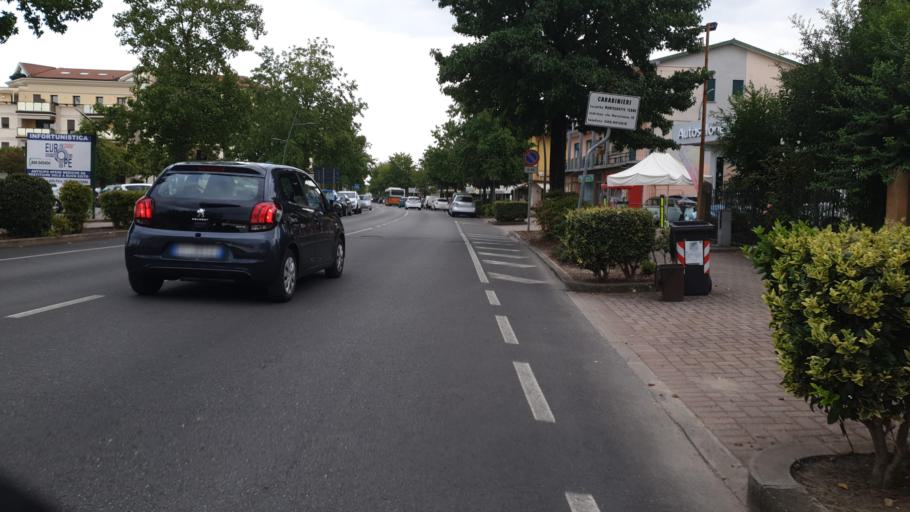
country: IT
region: Veneto
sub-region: Provincia di Padova
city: Montegrotto Terme
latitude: 45.3436
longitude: 11.7771
